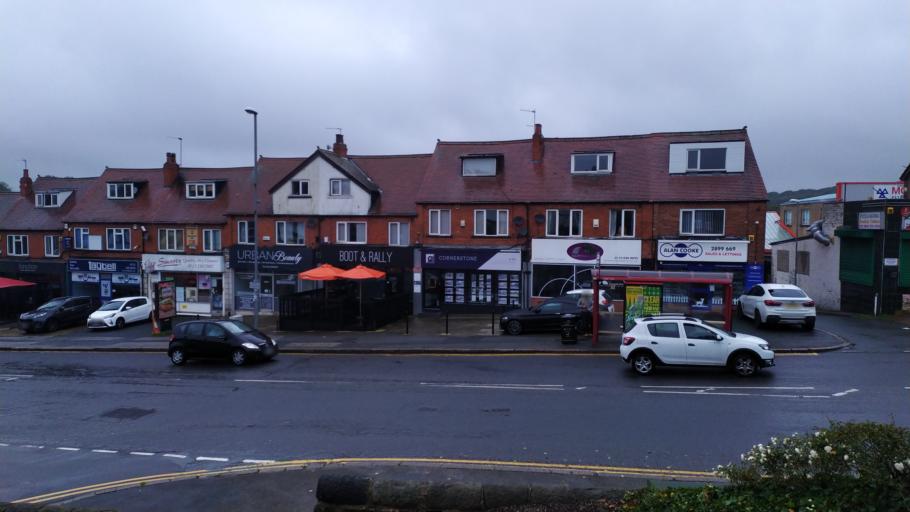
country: GB
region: England
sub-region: City and Borough of Leeds
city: Chapel Allerton
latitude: 53.8287
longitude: -1.5657
